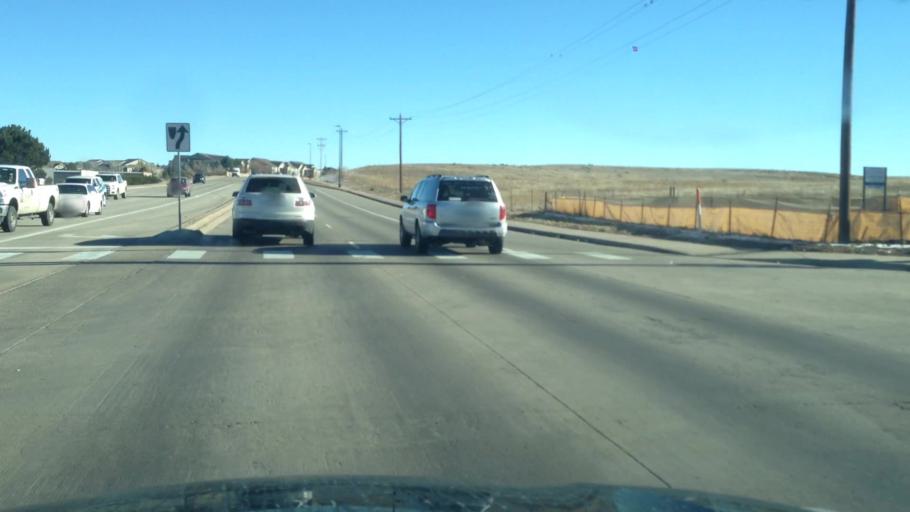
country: US
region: Colorado
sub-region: Arapahoe County
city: Dove Valley
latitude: 39.5821
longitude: -104.8127
